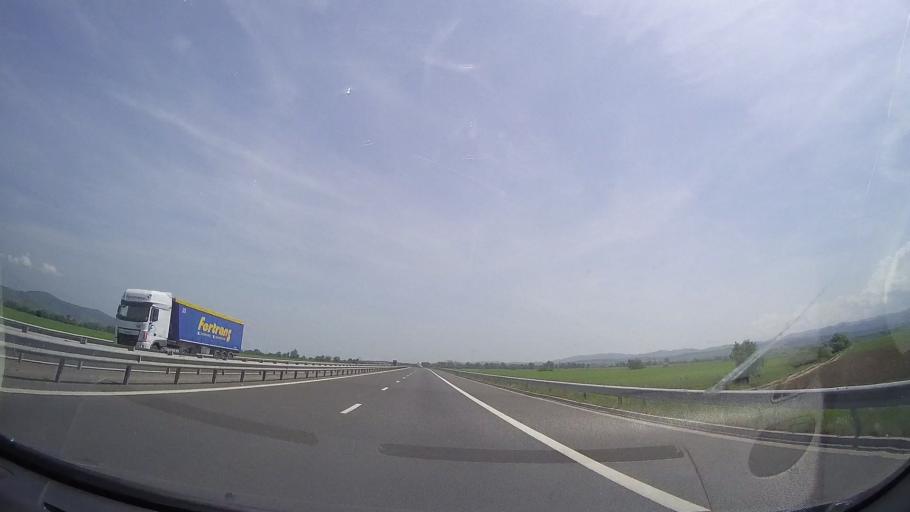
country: RO
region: Hunedoara
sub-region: Comuna Geoagiu
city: Geoagiu
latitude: 45.8828
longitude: 23.2242
